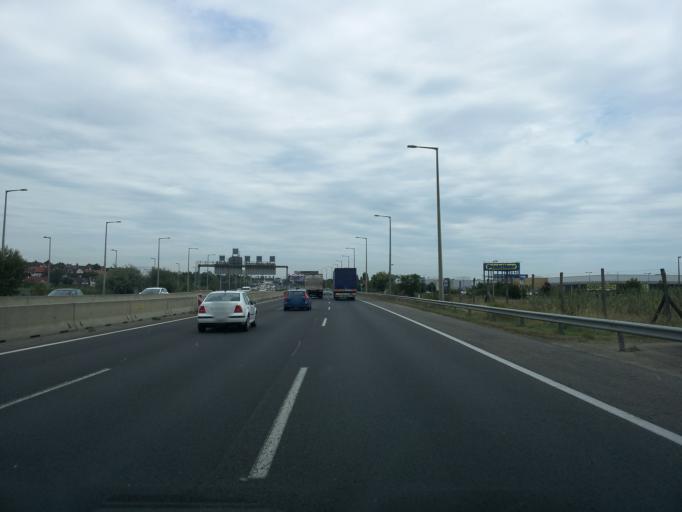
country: HU
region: Pest
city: Budaors
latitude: 47.4532
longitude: 18.9679
